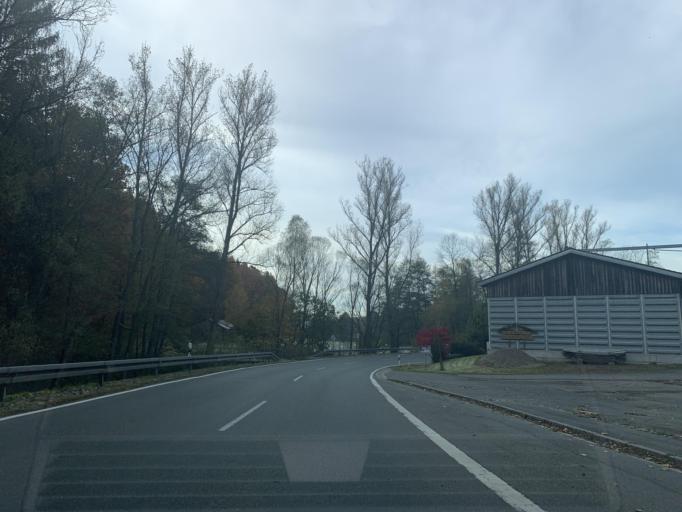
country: DE
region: Bavaria
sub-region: Upper Palatinate
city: Bach
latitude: 49.3813
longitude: 12.3808
